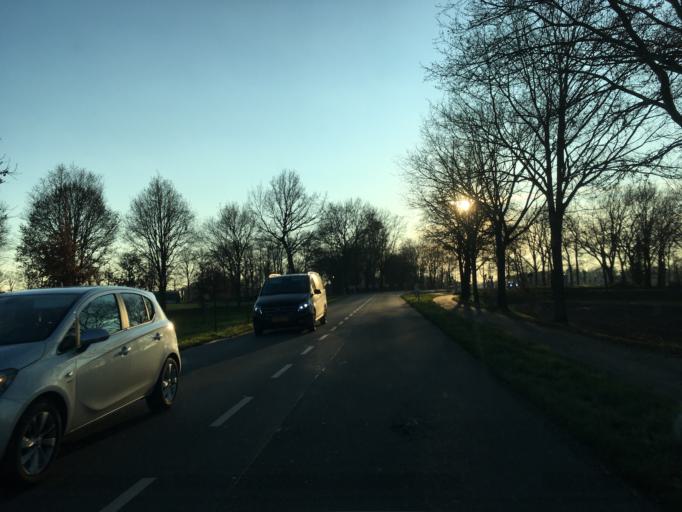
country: DE
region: North Rhine-Westphalia
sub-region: Regierungsbezirk Munster
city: Gronau
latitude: 52.1638
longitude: 7.0290
